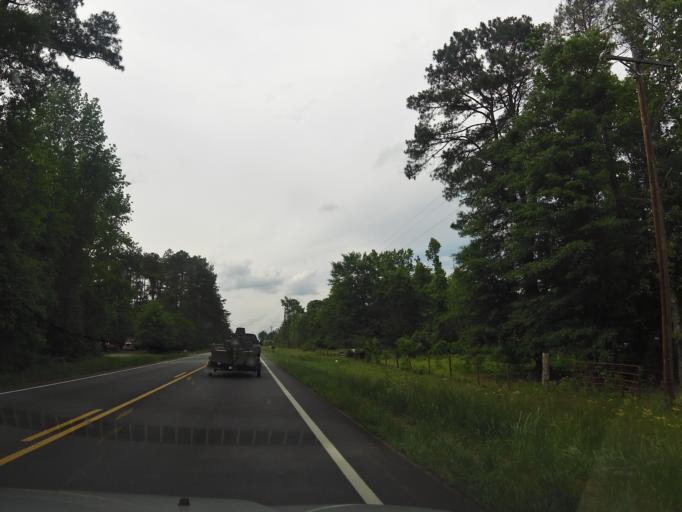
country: US
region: Georgia
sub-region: McDuffie County
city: Thomson
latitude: 33.4006
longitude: -82.4776
